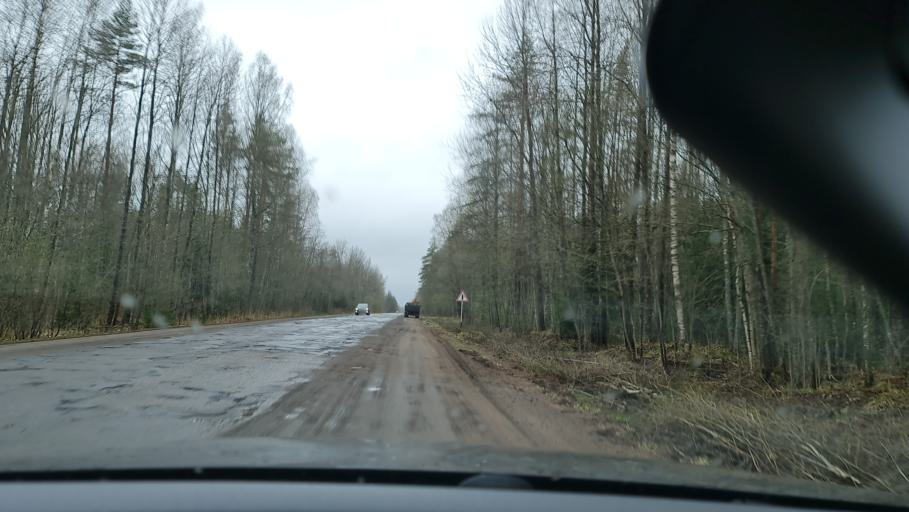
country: RU
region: Novgorod
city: Demyansk
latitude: 57.6732
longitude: 32.5478
